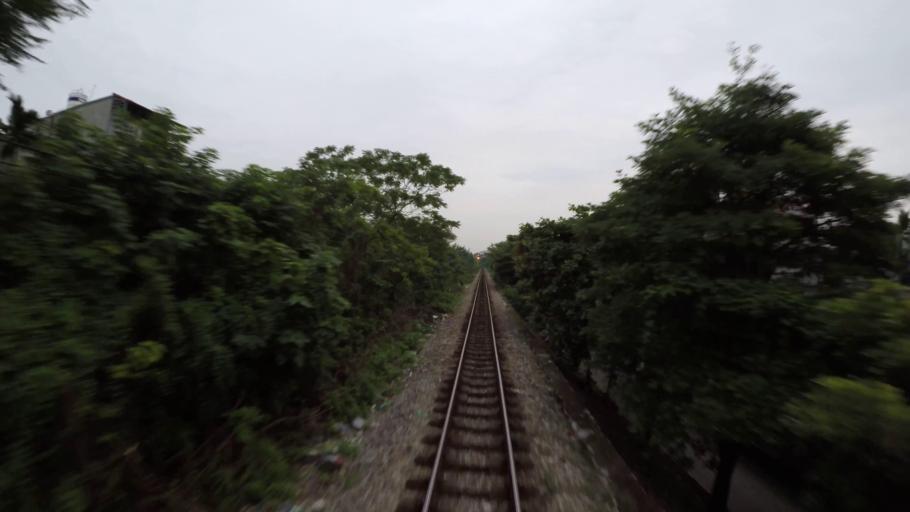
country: VN
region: Ha Noi
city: Trau Quy
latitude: 21.0419
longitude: 105.8968
